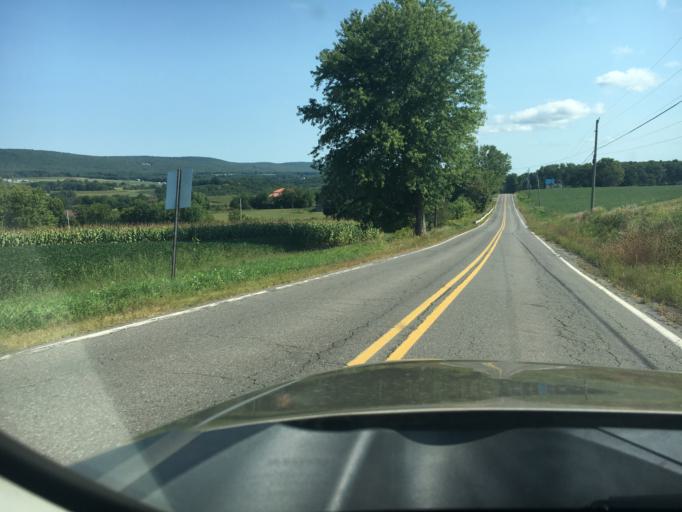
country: US
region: Pennsylvania
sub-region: Luzerne County
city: Conyngham
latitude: 41.0098
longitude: -76.0497
